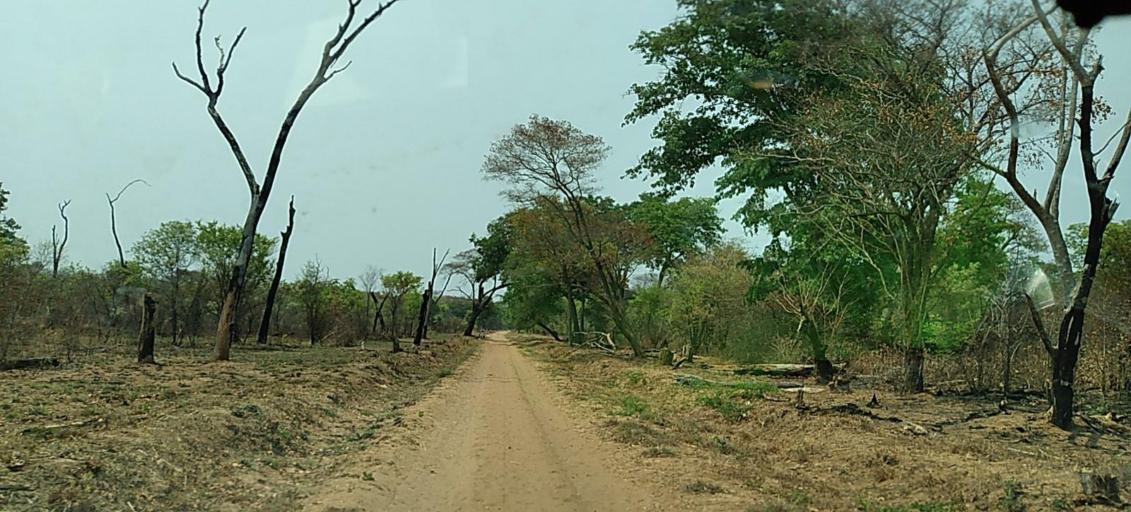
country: ZM
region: Western
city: Lukulu
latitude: -13.9886
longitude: 23.2304
